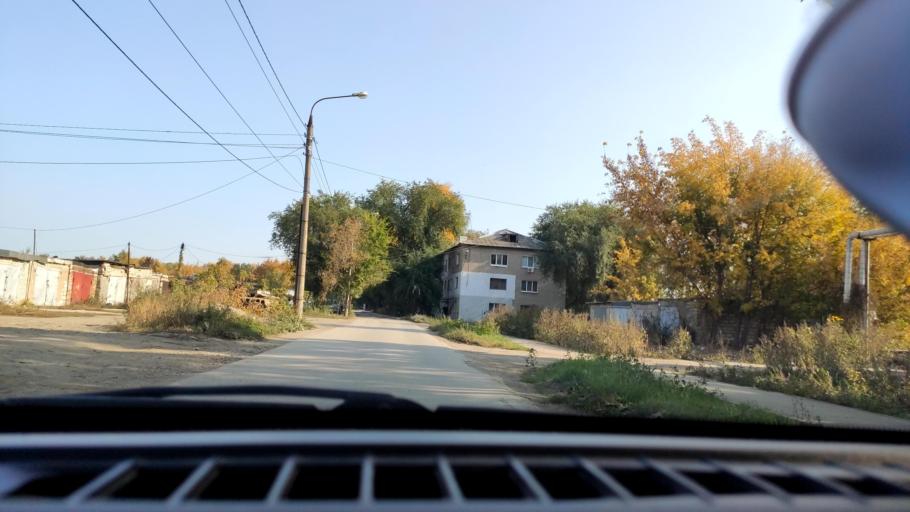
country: RU
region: Samara
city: Smyshlyayevka
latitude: 53.1893
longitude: 50.2831
